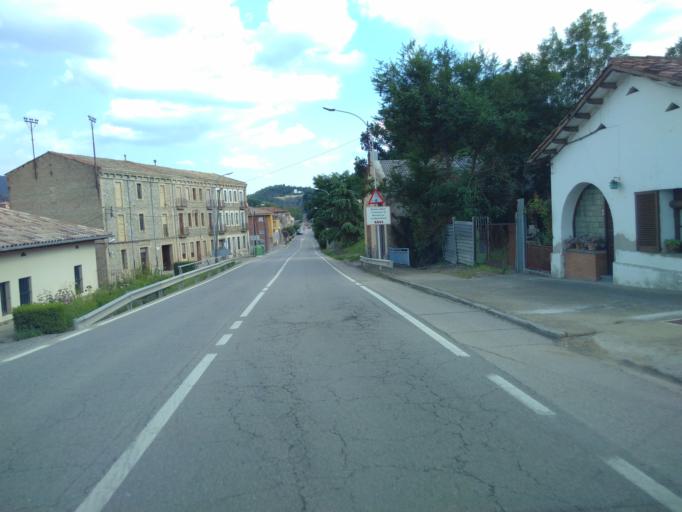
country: ES
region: Catalonia
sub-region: Provincia de Barcelona
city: Montesquiu
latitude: 42.1031
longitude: 2.2142
